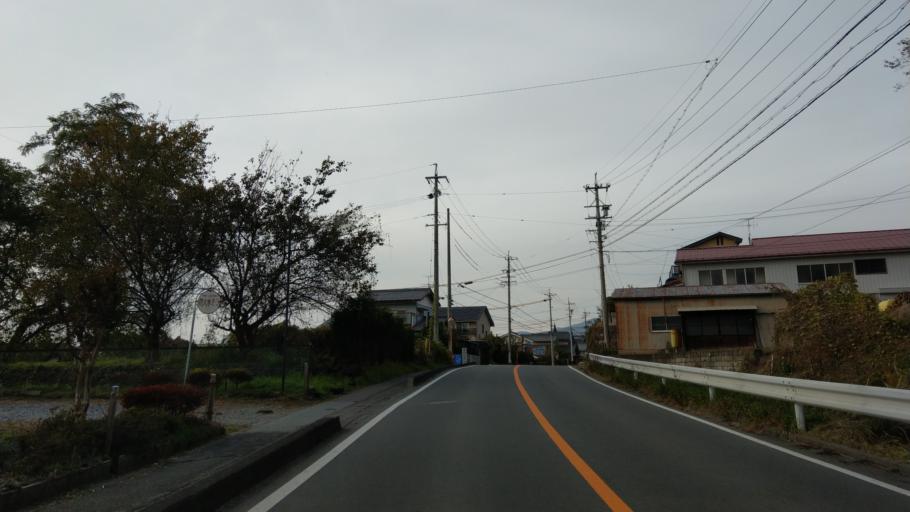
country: JP
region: Nagano
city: Komoro
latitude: 36.3194
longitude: 138.4281
